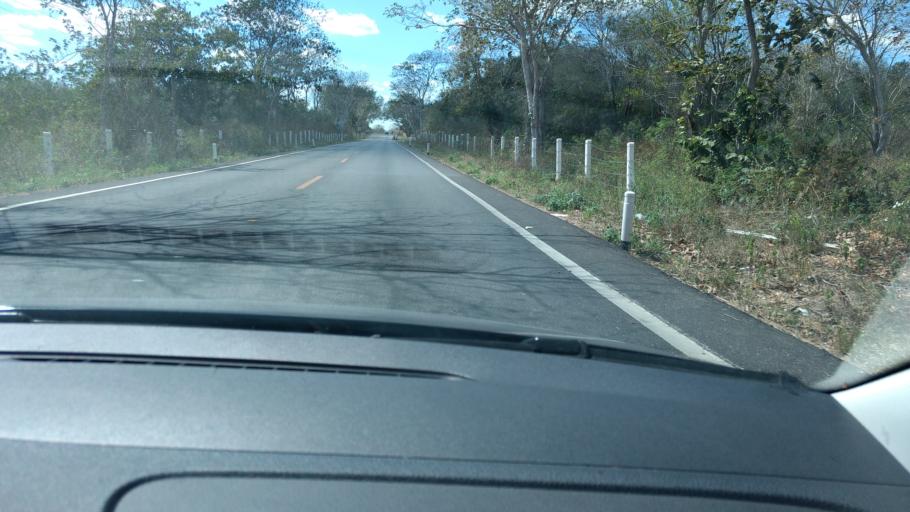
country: MX
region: Yucatan
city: Peto
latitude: 20.1176
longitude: -88.9504
